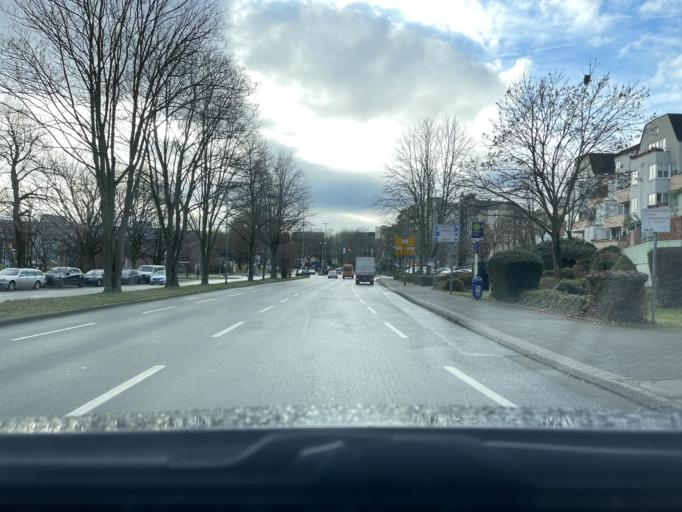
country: DE
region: North Rhine-Westphalia
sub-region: Regierungsbezirk Munster
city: Bottrop
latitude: 51.4736
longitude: 6.9562
